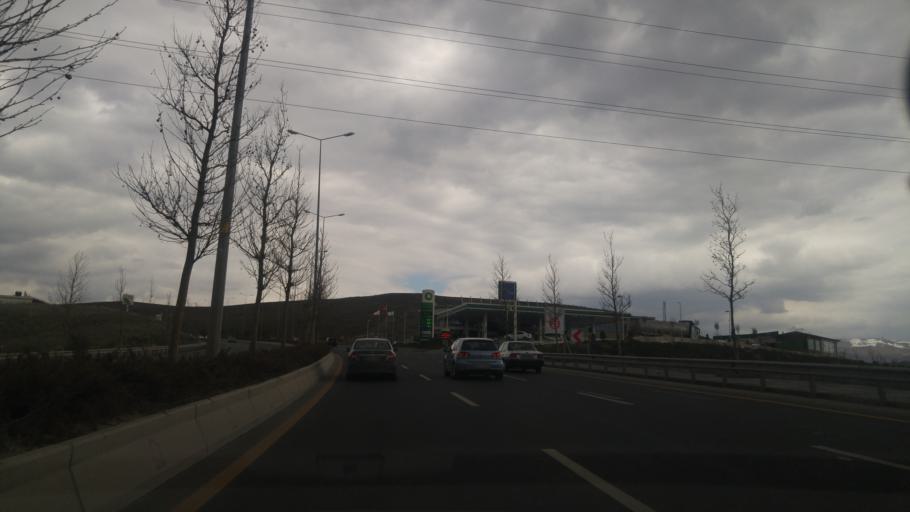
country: TR
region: Ankara
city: Mamak
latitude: 39.8849
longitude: 32.9176
